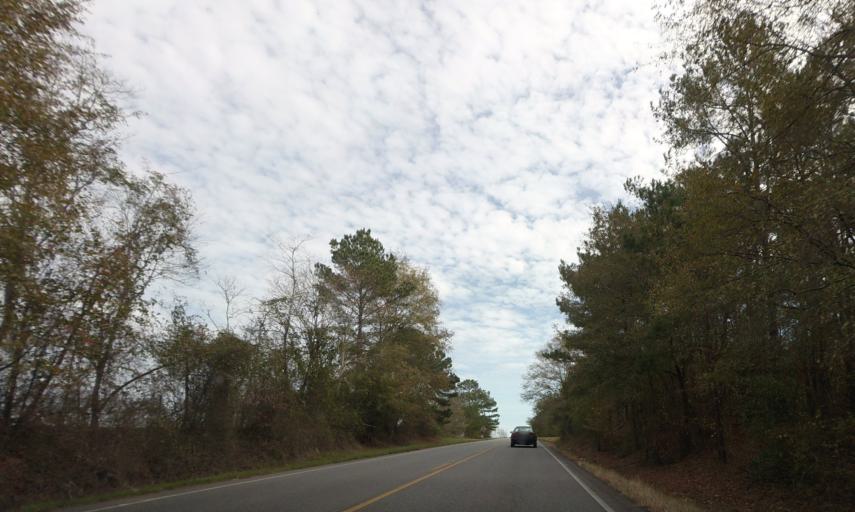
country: US
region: Georgia
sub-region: Dodge County
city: Chester
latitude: 32.4101
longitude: -83.2353
